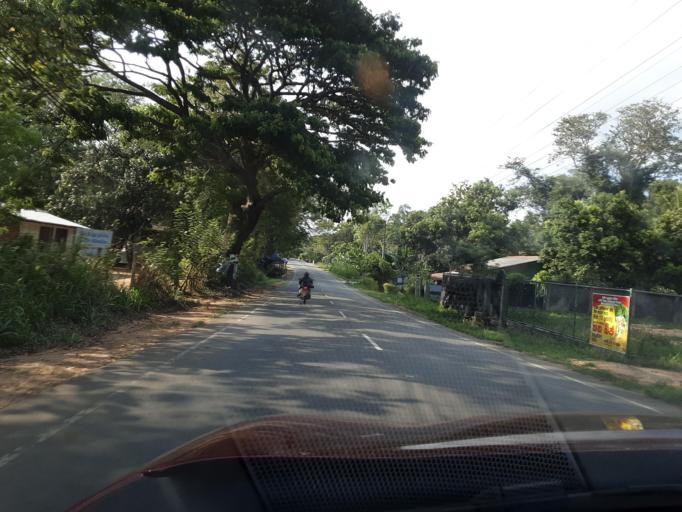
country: LK
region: Uva
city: Haputale
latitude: 6.6749
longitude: 81.1119
